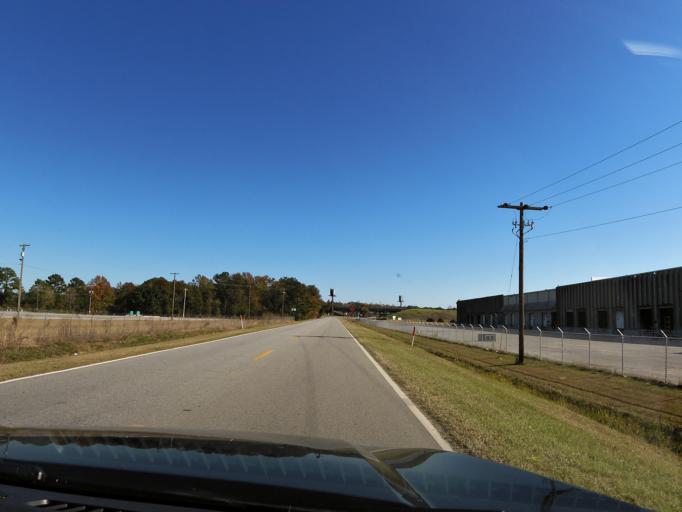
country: US
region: Georgia
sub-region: Chatham County
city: Savannah
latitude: 32.0679
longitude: -81.1408
